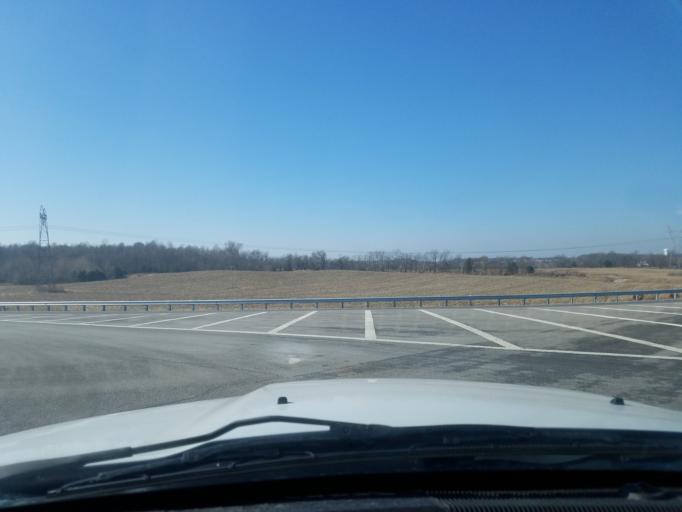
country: US
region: Kentucky
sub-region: Hardin County
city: Elizabethtown
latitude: 37.6549
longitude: -85.8903
